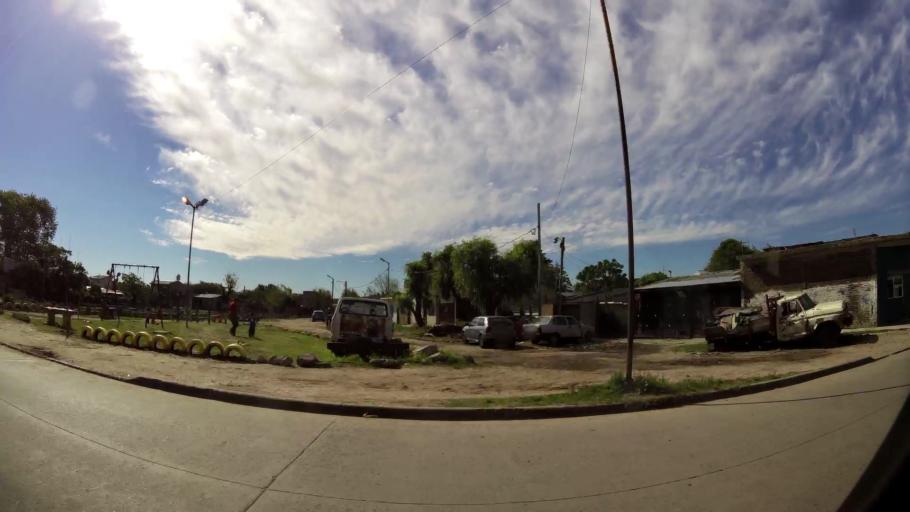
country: AR
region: Buenos Aires
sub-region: Partido de Quilmes
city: Quilmes
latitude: -34.7680
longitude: -58.3045
